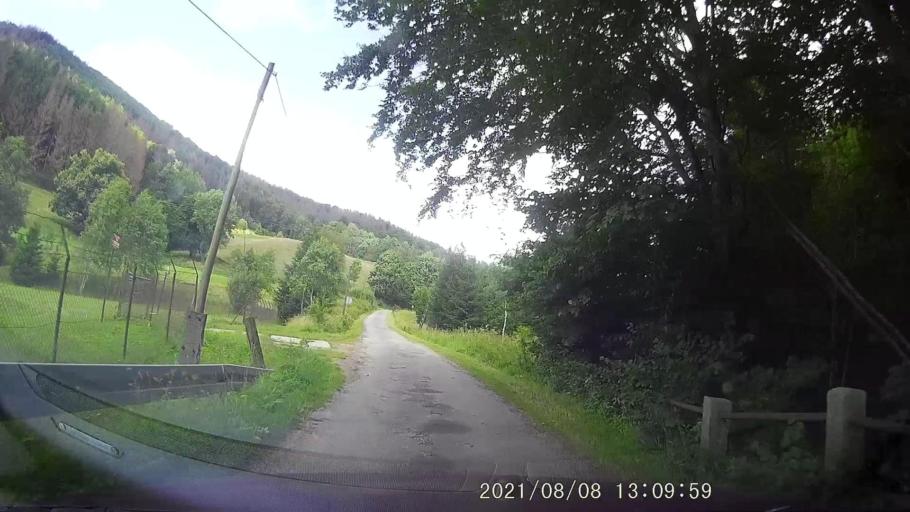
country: PL
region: Lower Silesian Voivodeship
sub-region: Powiat klodzki
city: Lewin Klodzki
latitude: 50.4385
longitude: 16.3089
